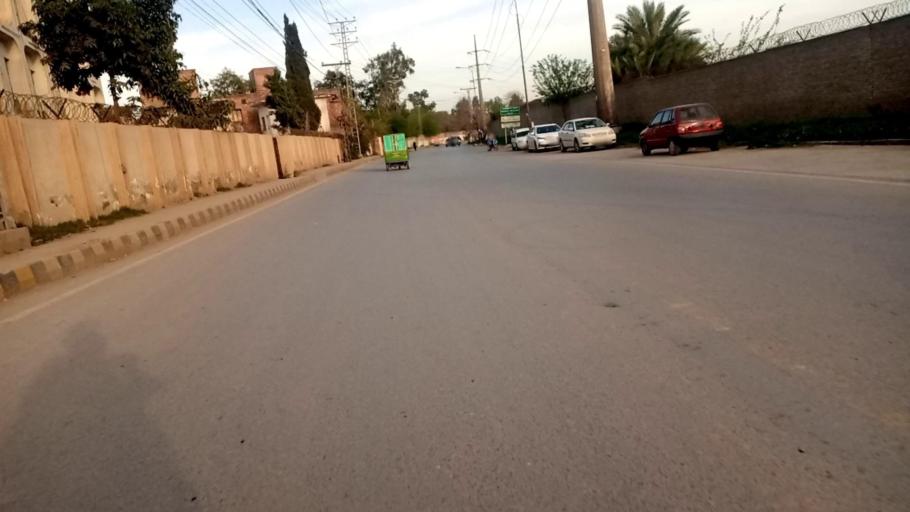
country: PK
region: Khyber Pakhtunkhwa
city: Peshawar
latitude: 34.0223
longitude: 71.5619
